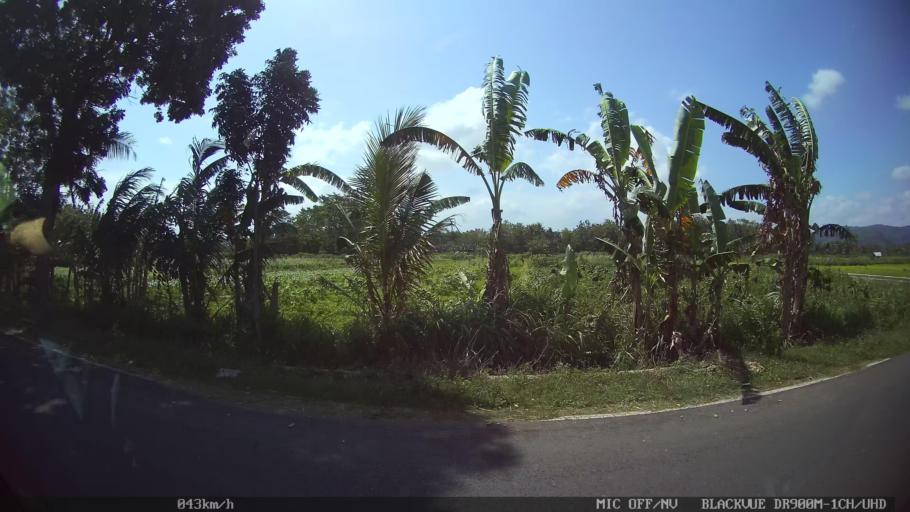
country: ID
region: Daerah Istimewa Yogyakarta
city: Pundong
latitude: -7.9569
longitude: 110.3695
